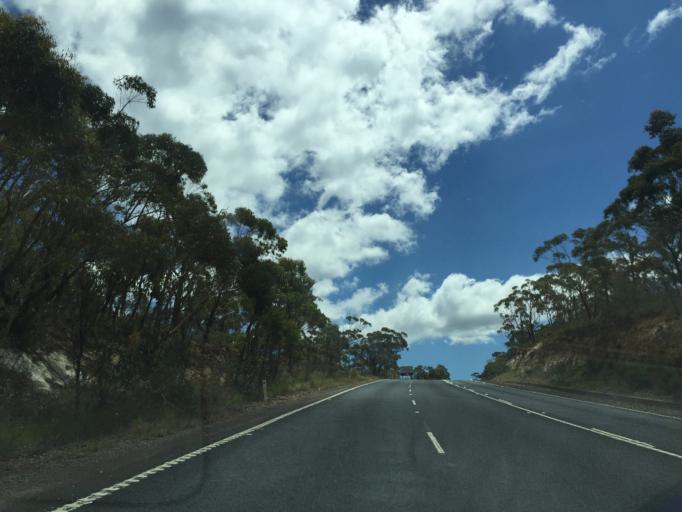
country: AU
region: New South Wales
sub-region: Blue Mountains Municipality
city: Blackheath
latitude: -33.5138
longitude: 150.2890
